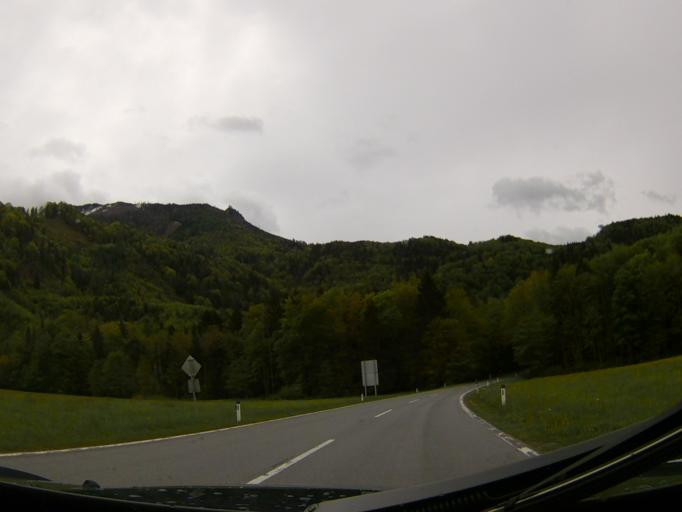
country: AT
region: Upper Austria
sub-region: Politischer Bezirk Vocklabruck
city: Innerschwand
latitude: 47.7964
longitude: 13.3991
